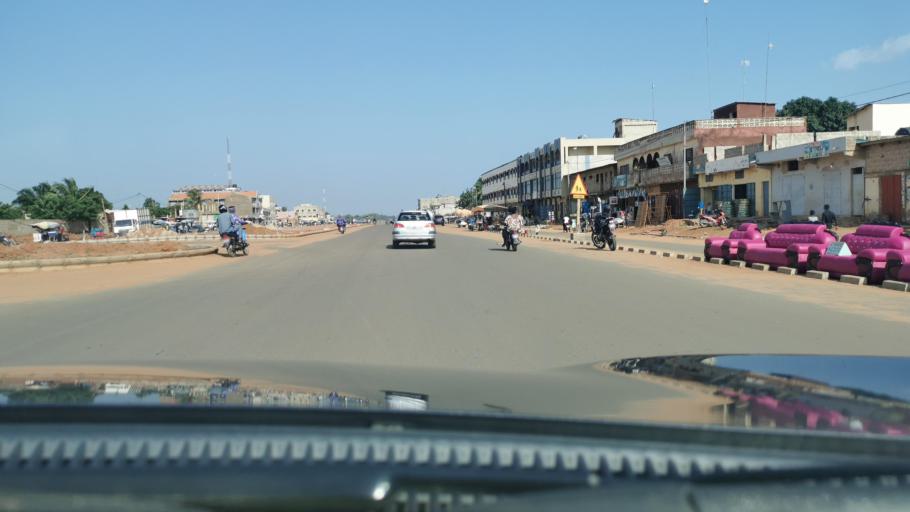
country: TG
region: Maritime
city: Lome
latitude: 6.2039
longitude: 1.1447
